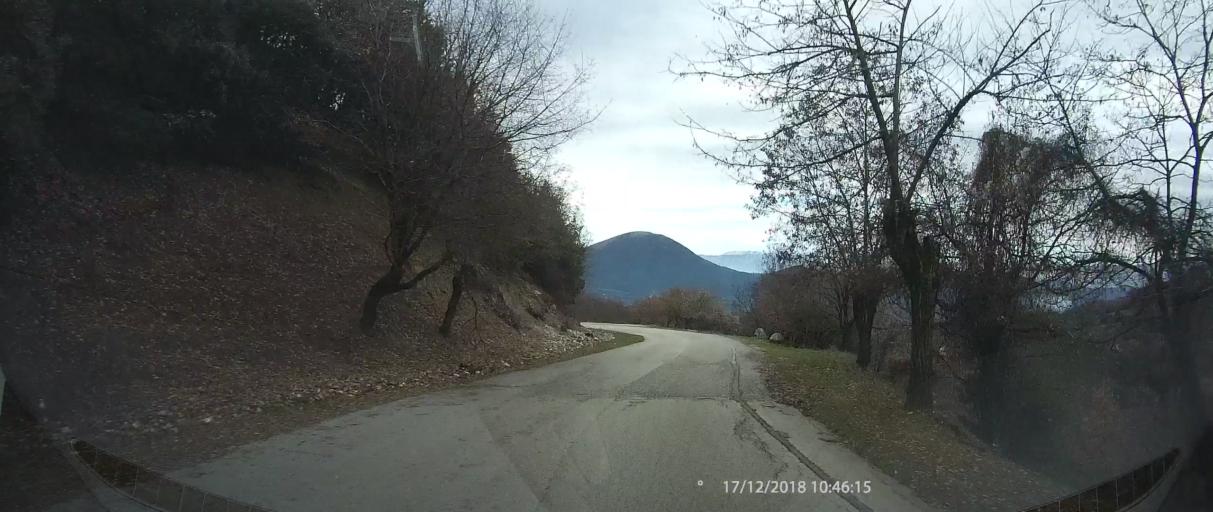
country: GR
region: Epirus
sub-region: Nomos Ioanninon
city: Konitsa
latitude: 39.9654
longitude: 20.7150
